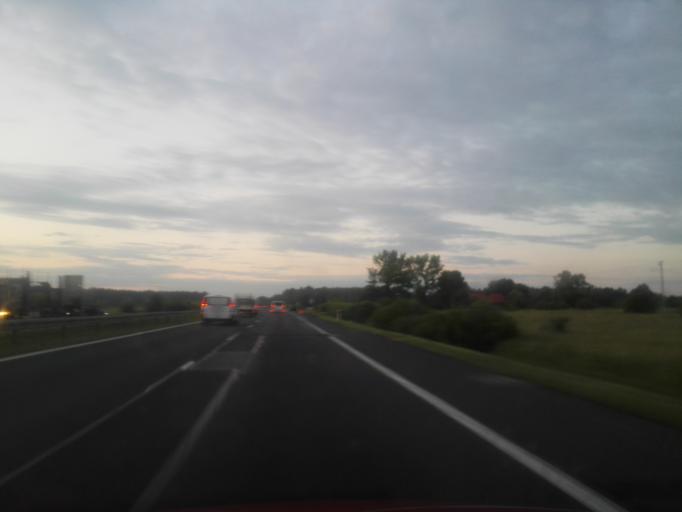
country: PL
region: Lodz Voivodeship
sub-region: Powiat radomszczanski
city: Kamiensk
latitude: 51.2352
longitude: 19.5164
